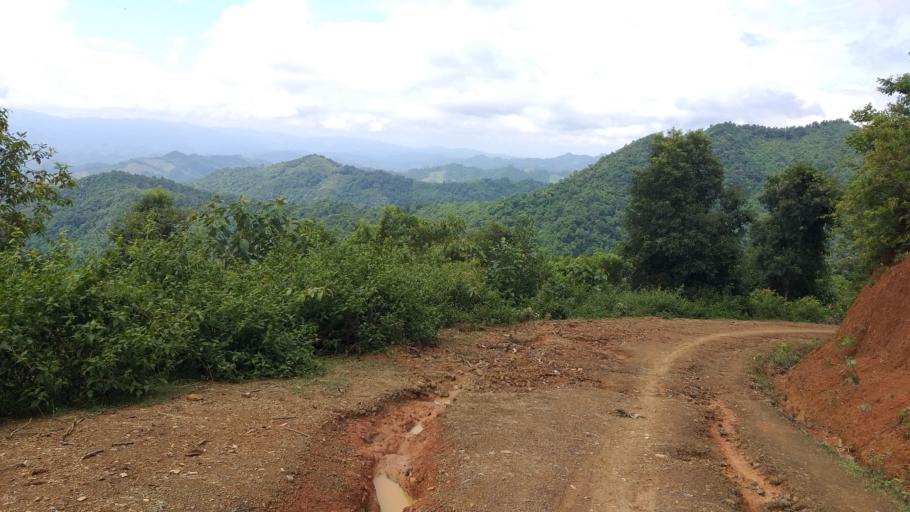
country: VN
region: Huyen Dien Bien
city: Dien Bien Phu
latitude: 21.4281
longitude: 102.6790
